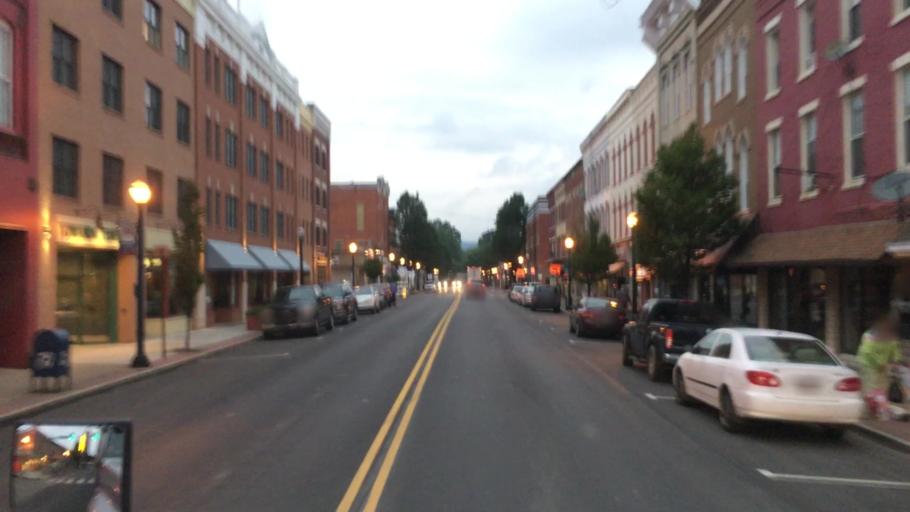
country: US
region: Pennsylvania
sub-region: Bradford County
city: Towanda
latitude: 41.7654
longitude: -76.4431
